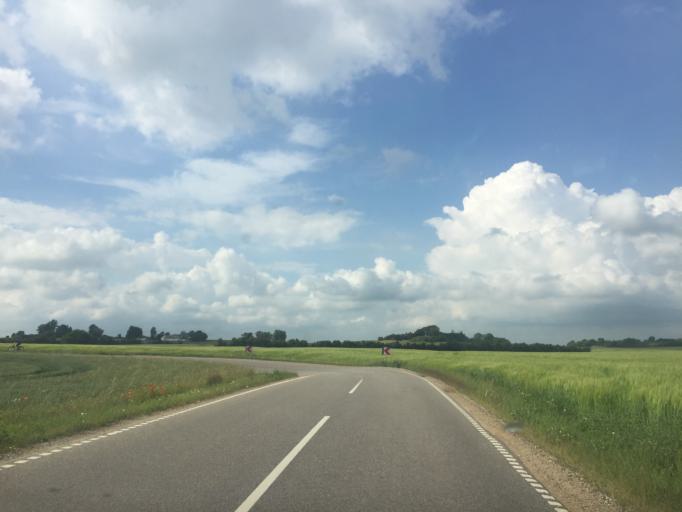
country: DK
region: Capital Region
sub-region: Hoje-Taastrup Kommune
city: Flong
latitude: 55.6864
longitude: 12.1885
